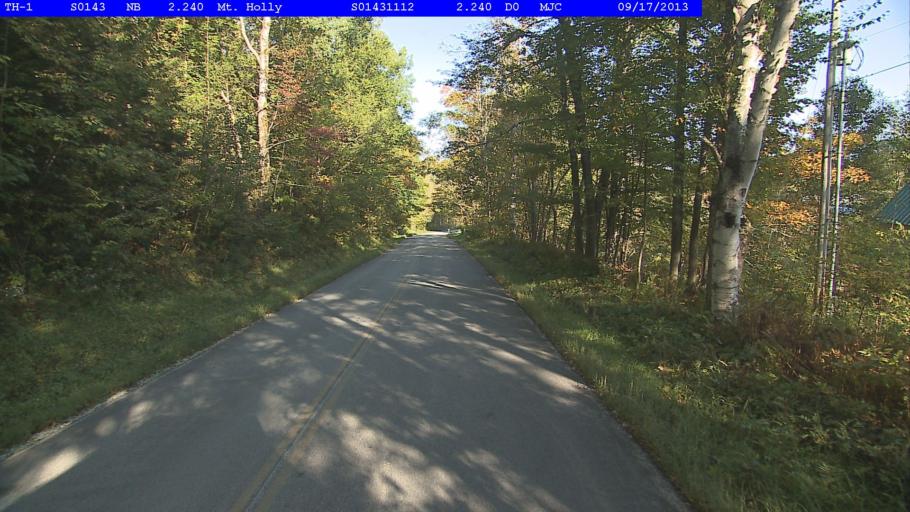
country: US
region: Vermont
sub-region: Rutland County
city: Rutland
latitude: 43.4306
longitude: -72.8227
